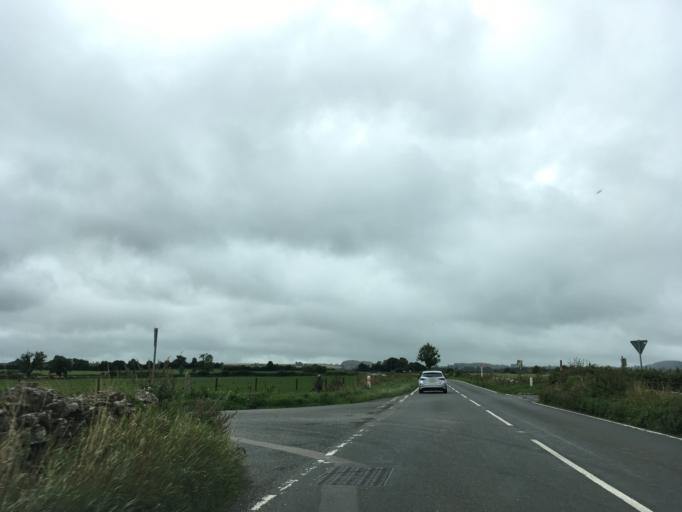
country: GB
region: England
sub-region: Bath and North East Somerset
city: Cameley
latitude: 51.2835
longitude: -2.5636
